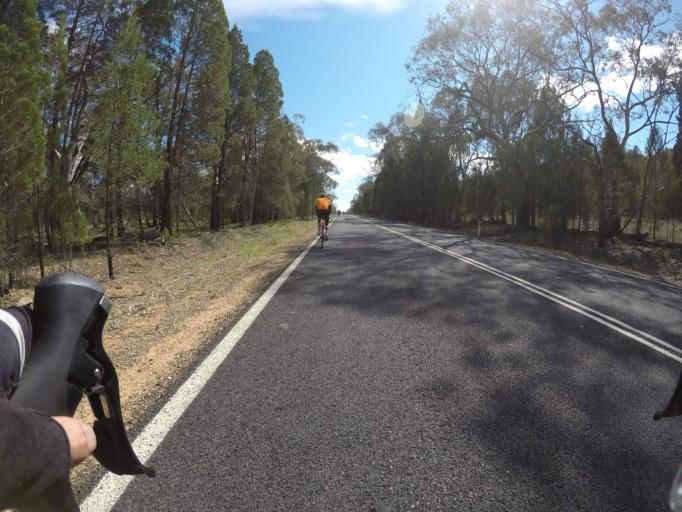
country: AU
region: New South Wales
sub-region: Parkes
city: Peak Hill
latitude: -32.6802
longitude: 148.5583
